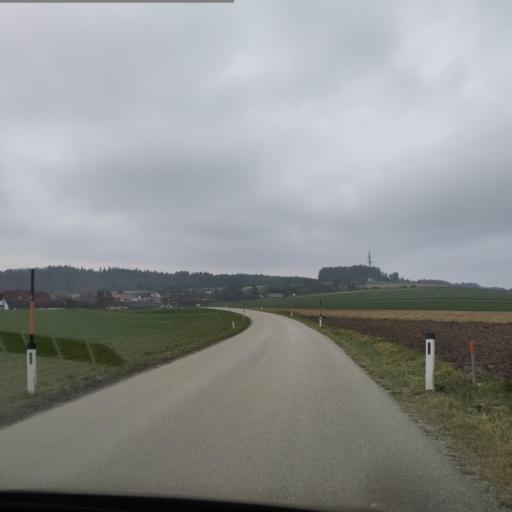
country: AT
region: Lower Austria
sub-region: Politischer Bezirk Sankt Polten
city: Hafnerbach
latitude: 48.2638
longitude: 15.5047
